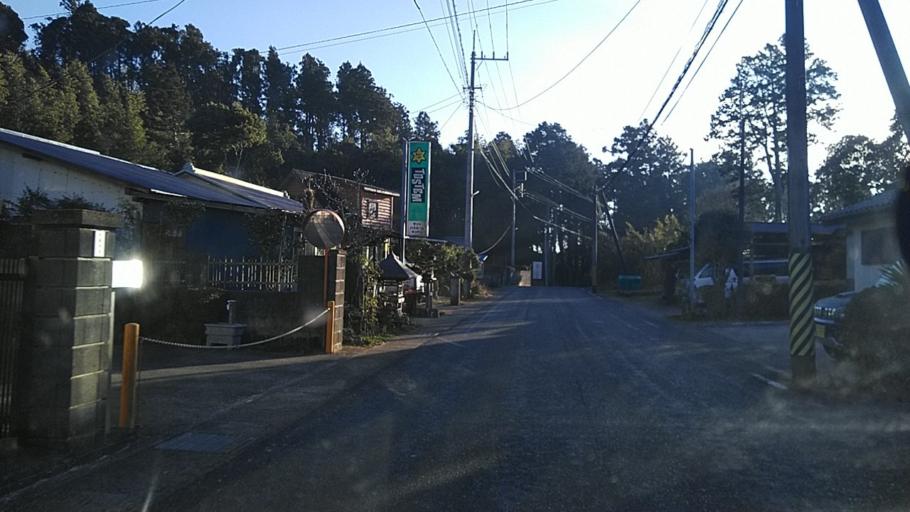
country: JP
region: Chiba
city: Kimitsu
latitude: 35.2548
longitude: 139.9613
